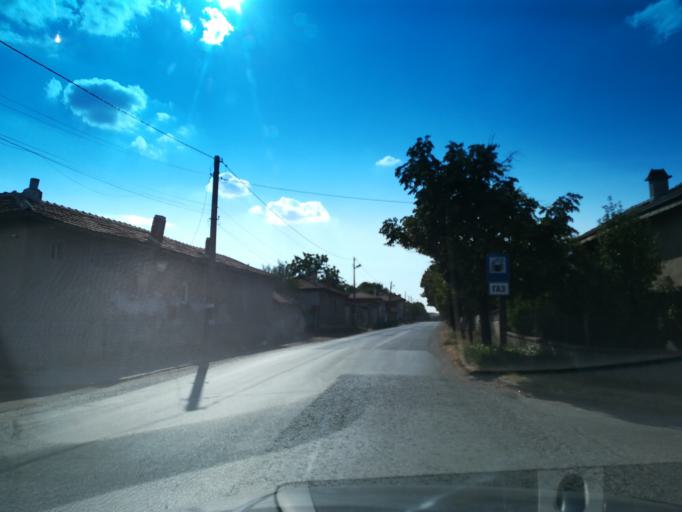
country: BG
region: Khaskovo
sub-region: Obshtina Mineralni Bani
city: Mineralni Bani
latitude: 42.0162
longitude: 25.4276
